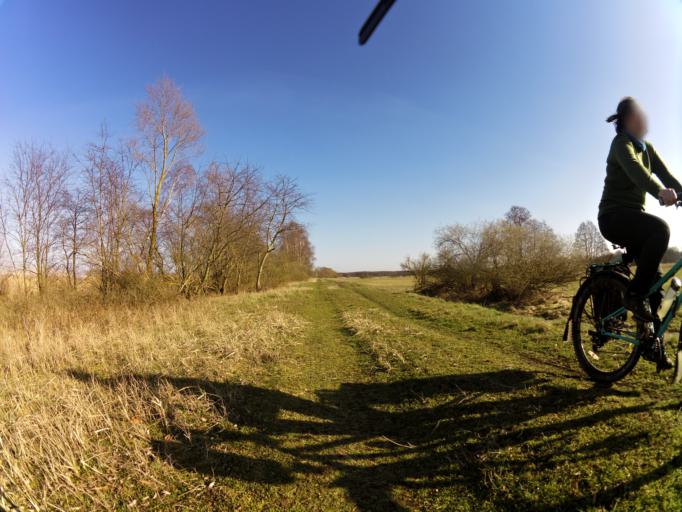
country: PL
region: West Pomeranian Voivodeship
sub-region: Powiat policki
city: Nowe Warpno
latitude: 53.6940
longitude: 14.3786
